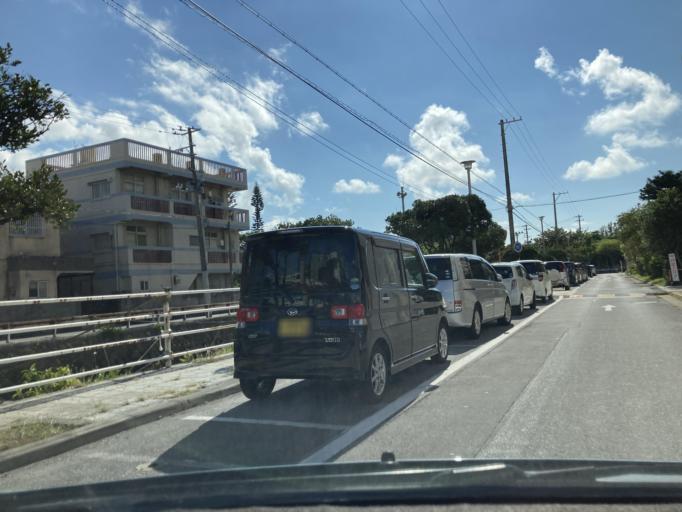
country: JP
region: Okinawa
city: Naha-shi
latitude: 26.2244
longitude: 127.6790
